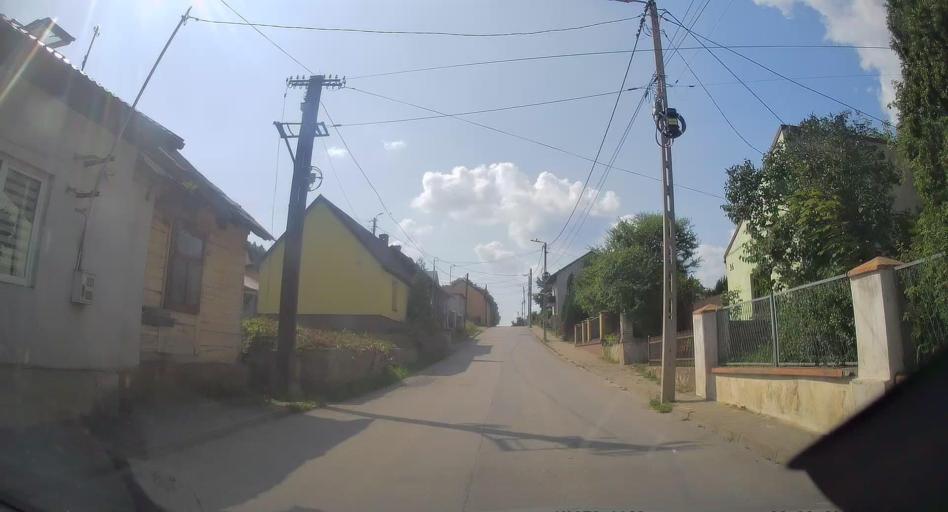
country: PL
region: Swietokrzyskie
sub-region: Powiat kielecki
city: Checiny
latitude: 50.8017
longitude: 20.4574
